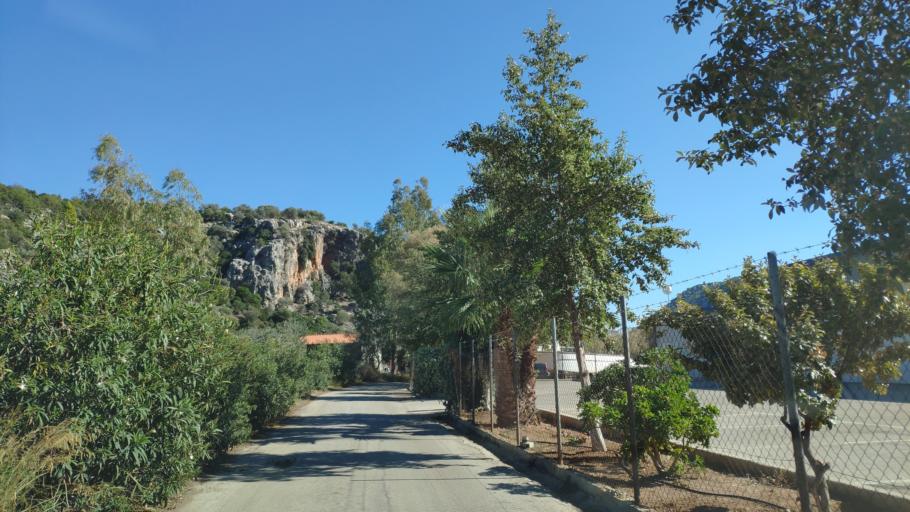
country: GR
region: Peloponnese
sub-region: Nomos Korinthias
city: Sofikon
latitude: 37.7334
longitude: 23.1172
